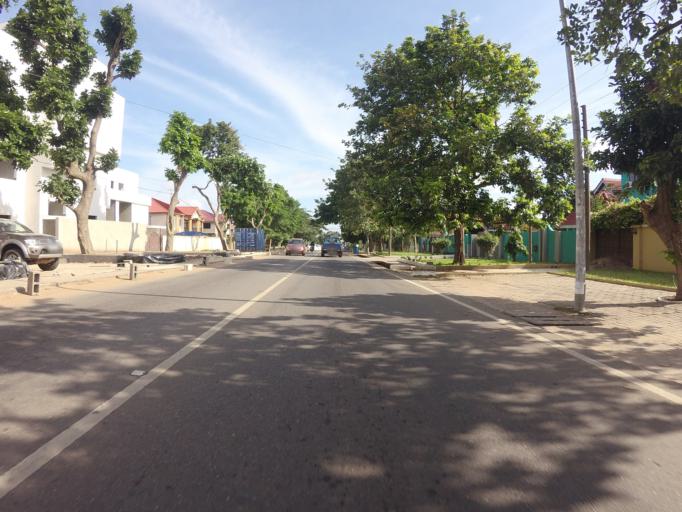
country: GH
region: Greater Accra
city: Medina Estates
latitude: 5.6326
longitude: -0.1609
